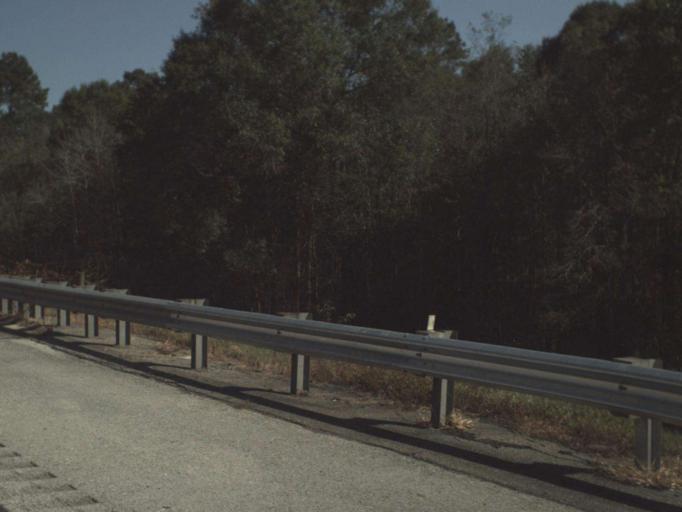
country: US
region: Florida
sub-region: Holmes County
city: Bonifay
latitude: 30.7591
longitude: -85.8052
